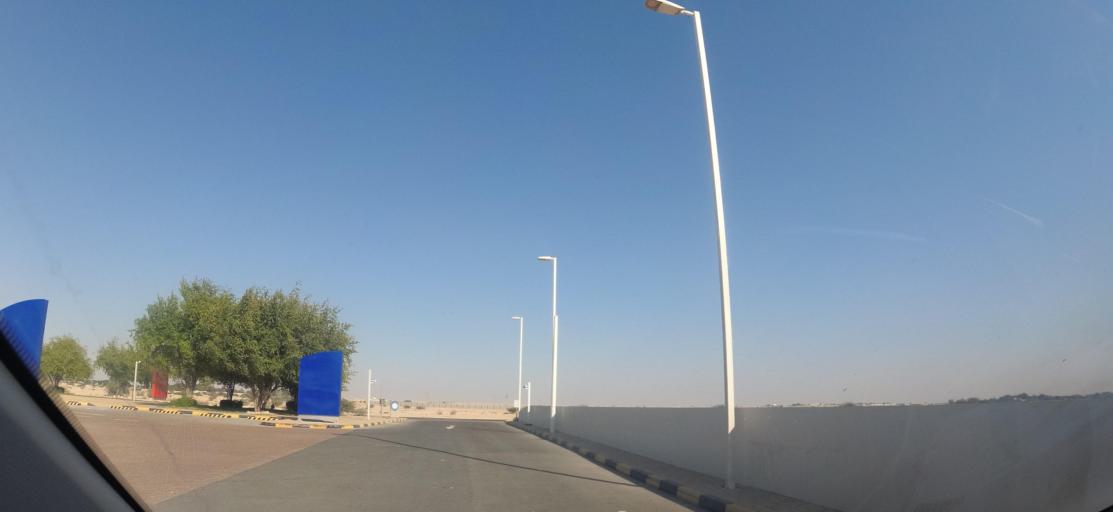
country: QA
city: Al Jumayliyah
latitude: 25.6168
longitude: 51.0861
